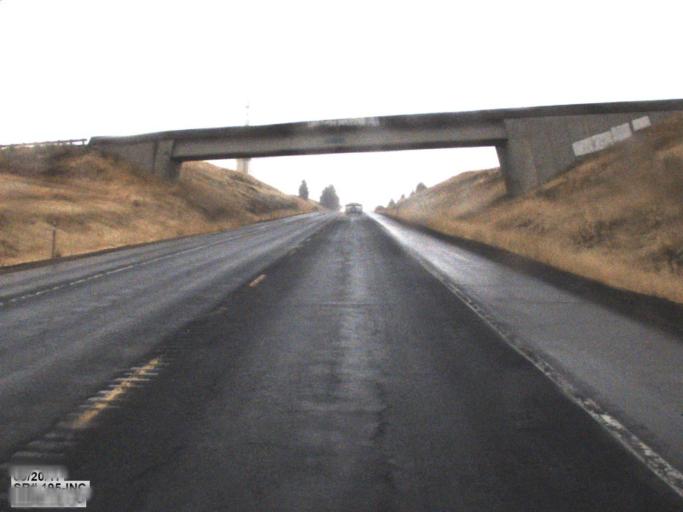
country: US
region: Washington
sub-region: Spokane County
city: Cheney
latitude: 47.2323
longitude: -117.3583
